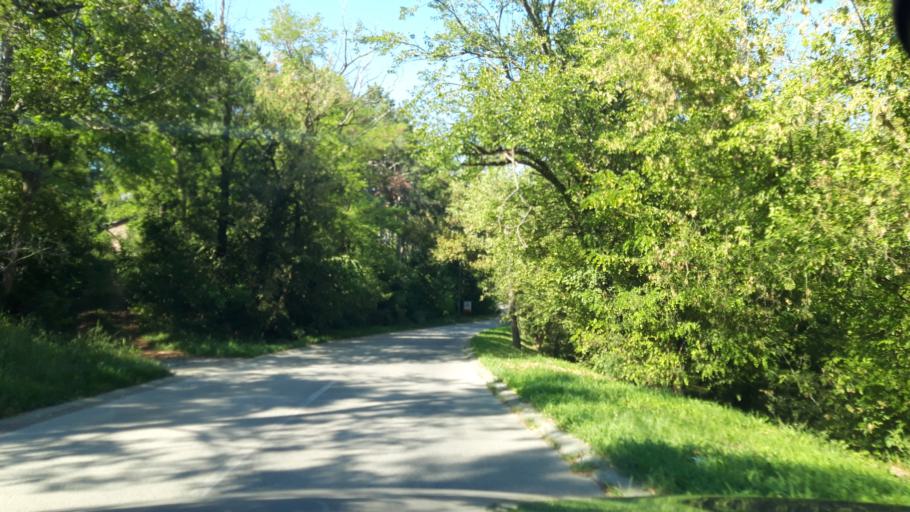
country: RS
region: Autonomna Pokrajina Vojvodina
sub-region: Sremski Okrug
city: Ruma
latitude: 45.0288
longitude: 19.8201
